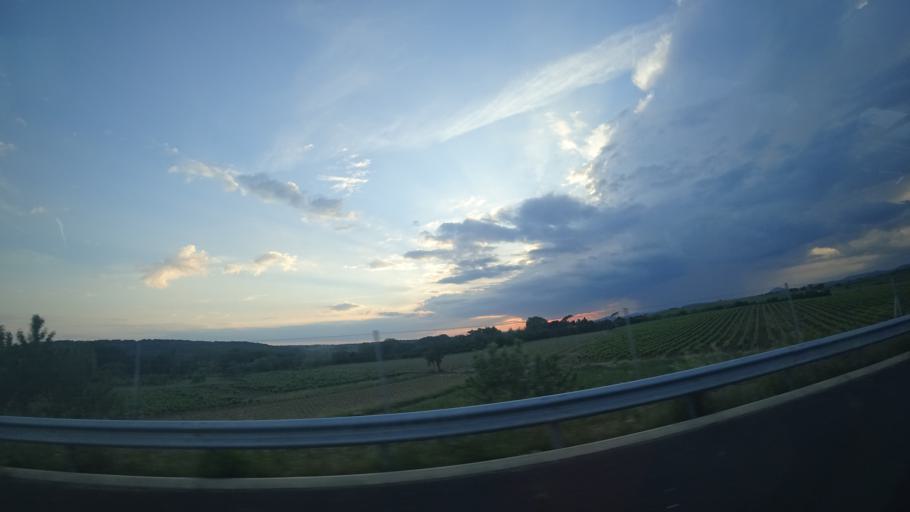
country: FR
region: Languedoc-Roussillon
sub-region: Departement de l'Herault
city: Lezignan-la-Cebe
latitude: 43.5135
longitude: 3.4432
